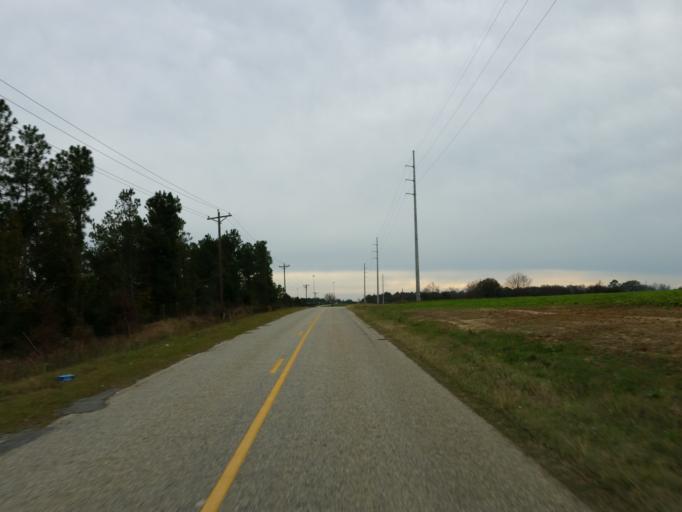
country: US
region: Georgia
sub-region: Dooly County
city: Vienna
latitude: 32.1288
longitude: -83.7613
